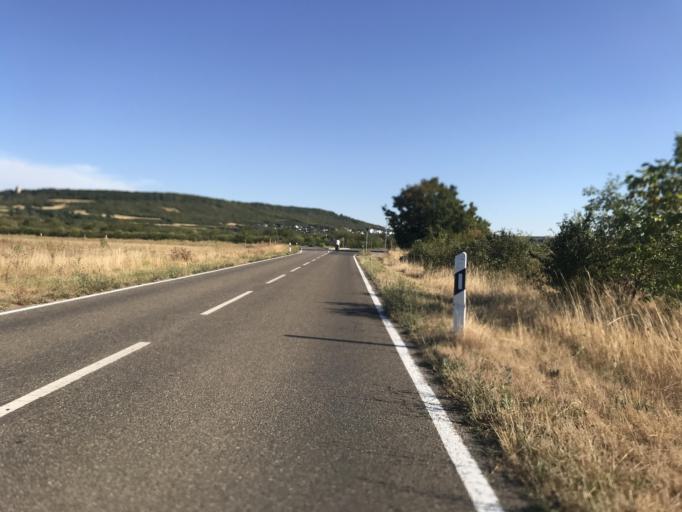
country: DE
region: Rheinland-Pfalz
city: Gau-Algesheim
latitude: 49.9714
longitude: 8.0121
